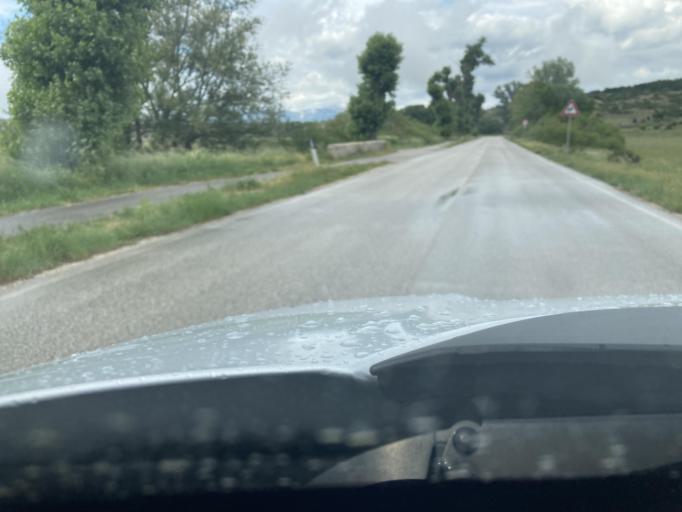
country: IT
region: Abruzzo
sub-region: Provincia dell' Aquila
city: Rocca di Mezzo
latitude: 42.2191
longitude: 13.5316
